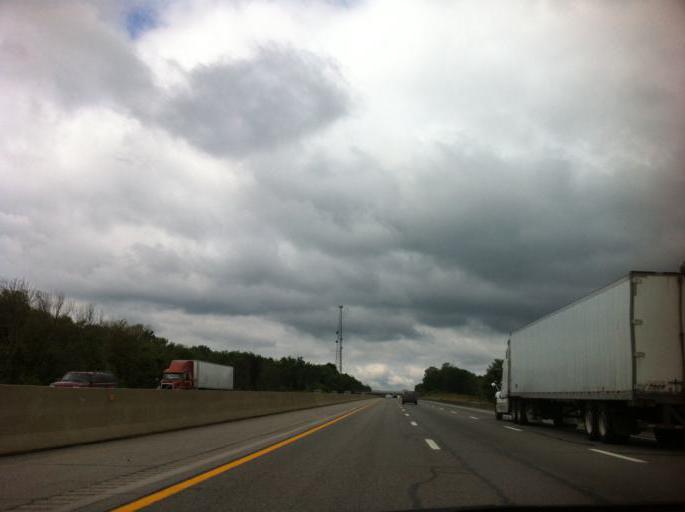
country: US
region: Ohio
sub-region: Portage County
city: Mantua
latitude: 41.2438
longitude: -81.2038
